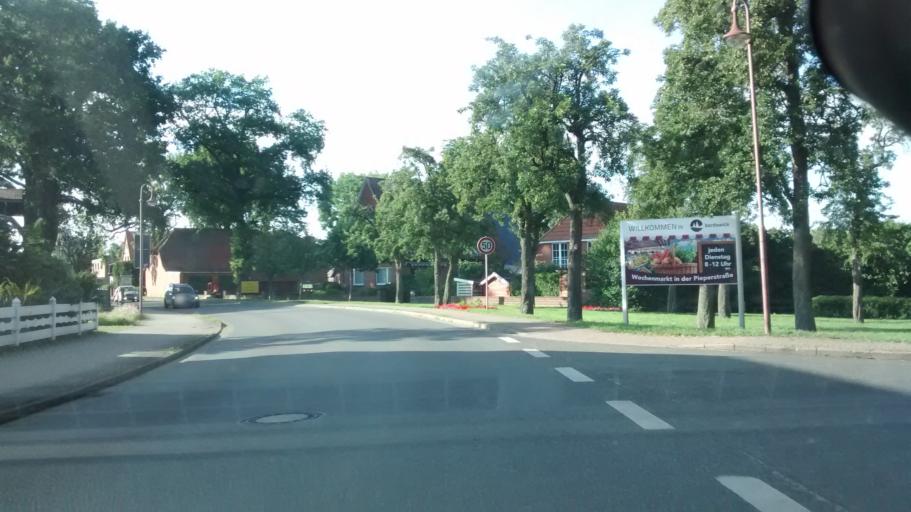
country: DE
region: Lower Saxony
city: Bardowick
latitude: 53.2925
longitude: 10.3954
